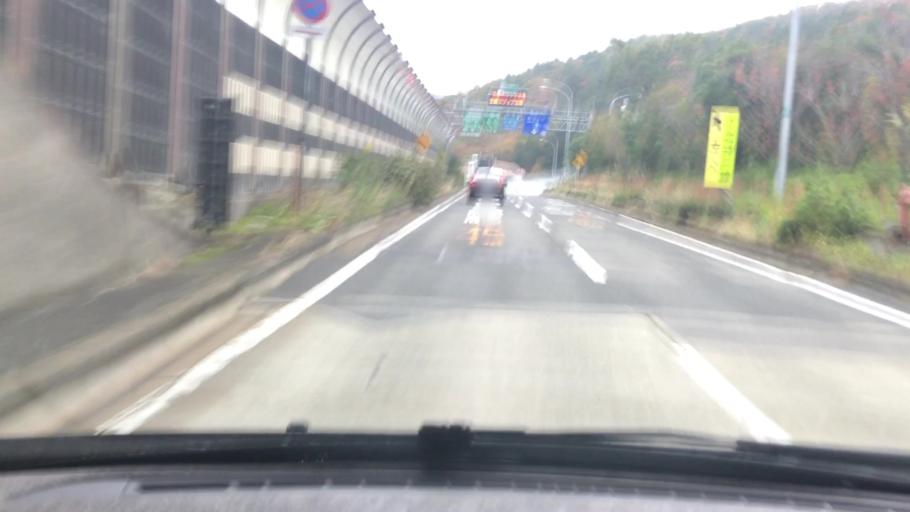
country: JP
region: Hyogo
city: Kobe
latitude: 34.7565
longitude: 135.1608
